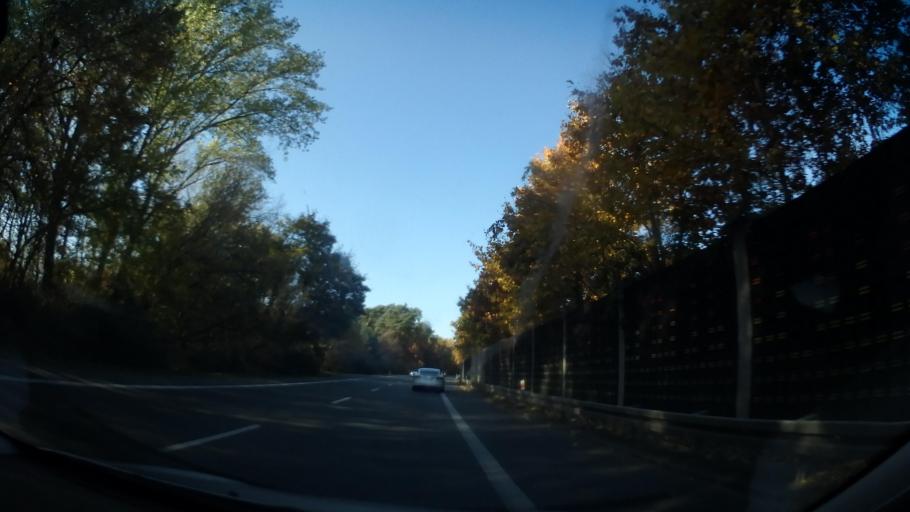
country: CZ
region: Pardubicky
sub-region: Okres Pardubice
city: Pardubice
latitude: 50.0196
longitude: 15.7558
